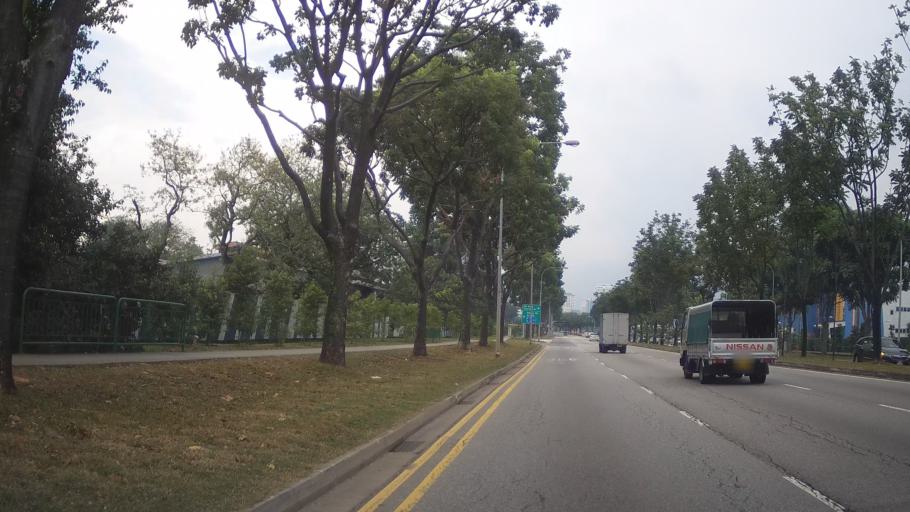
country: MY
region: Johor
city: Johor Bahru
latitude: 1.3339
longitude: 103.7081
